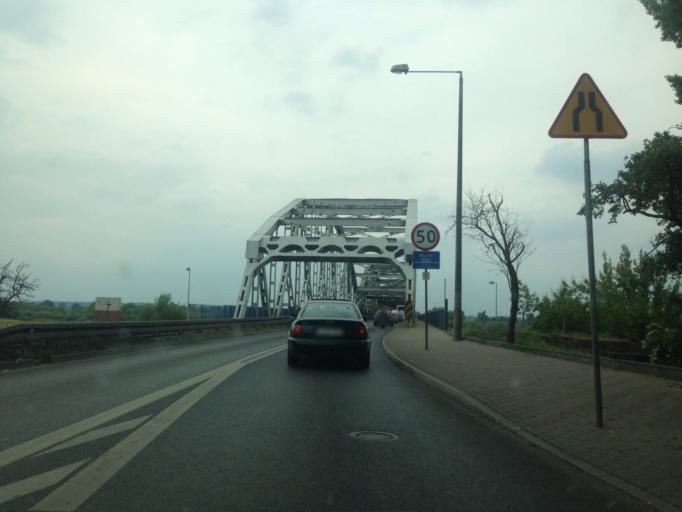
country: PL
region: Kujawsko-Pomorskie
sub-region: Grudziadz
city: Grudziadz
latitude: 53.4828
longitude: 18.7449
